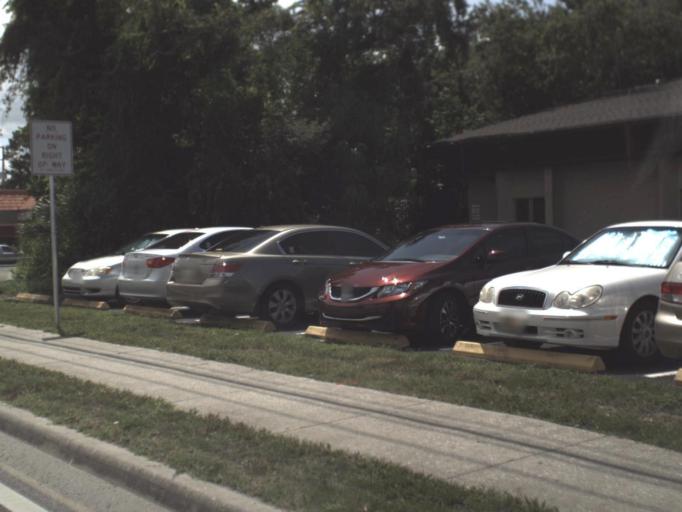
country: US
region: Florida
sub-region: Pasco County
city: Bayonet Point
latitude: 28.3312
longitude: -82.6927
